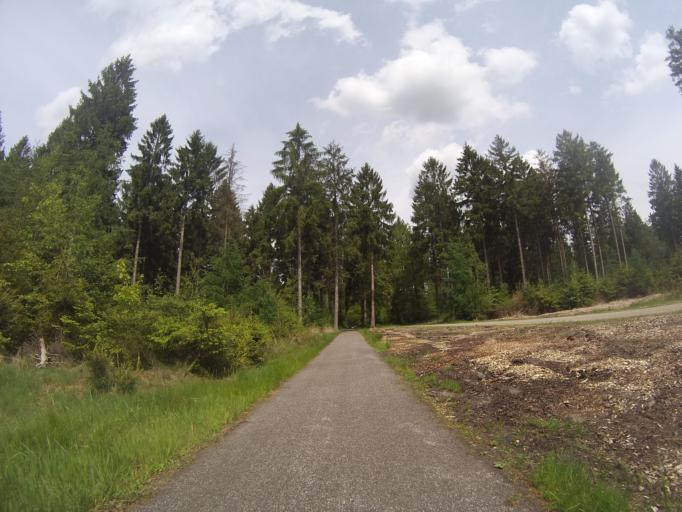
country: NL
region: Drenthe
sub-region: Gemeente Assen
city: Assen
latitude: 52.9067
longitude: 6.6533
